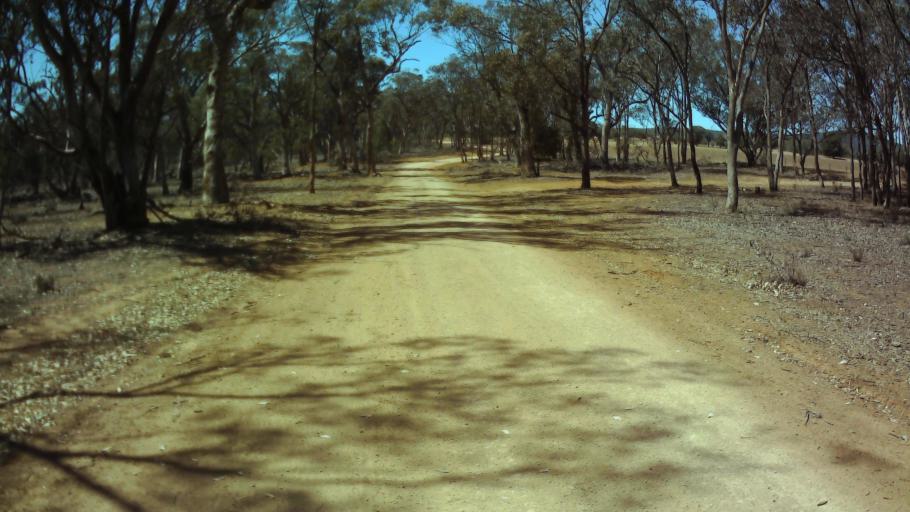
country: AU
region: New South Wales
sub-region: Weddin
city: Grenfell
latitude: -33.9411
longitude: 148.0783
